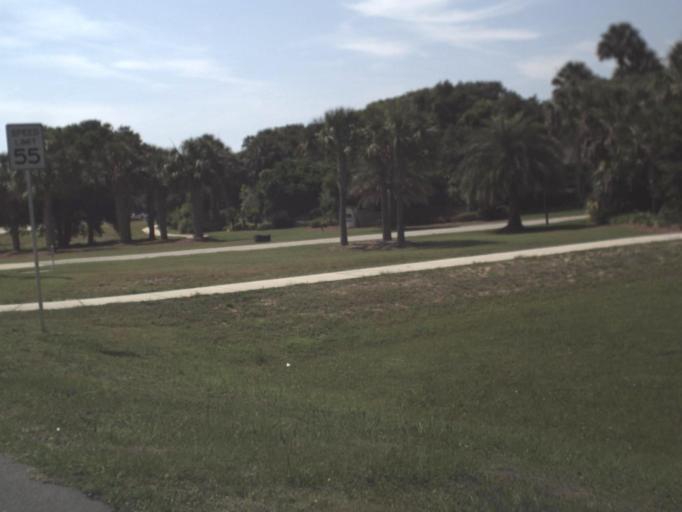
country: US
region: Florida
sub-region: Saint Johns County
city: Palm Valley
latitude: 30.1601
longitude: -81.3582
